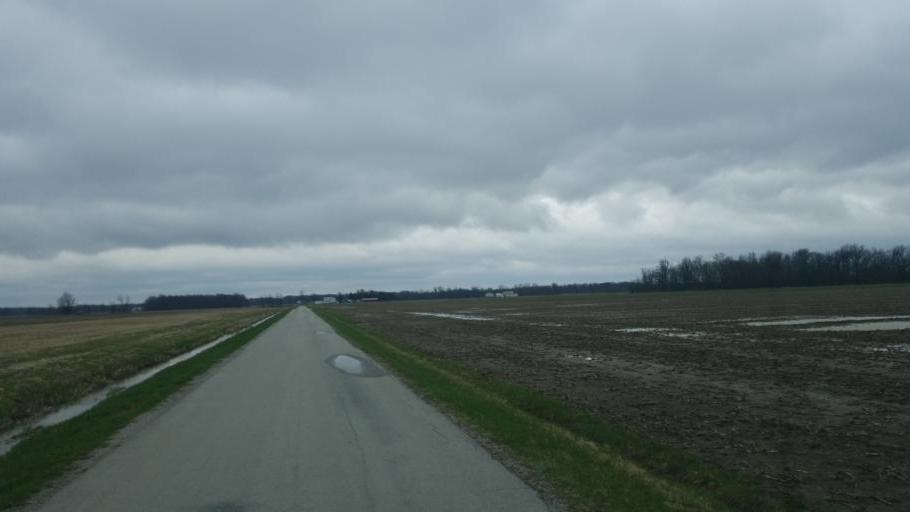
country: US
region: Ohio
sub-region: Hardin County
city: Forest
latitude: 40.7361
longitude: -83.4584
